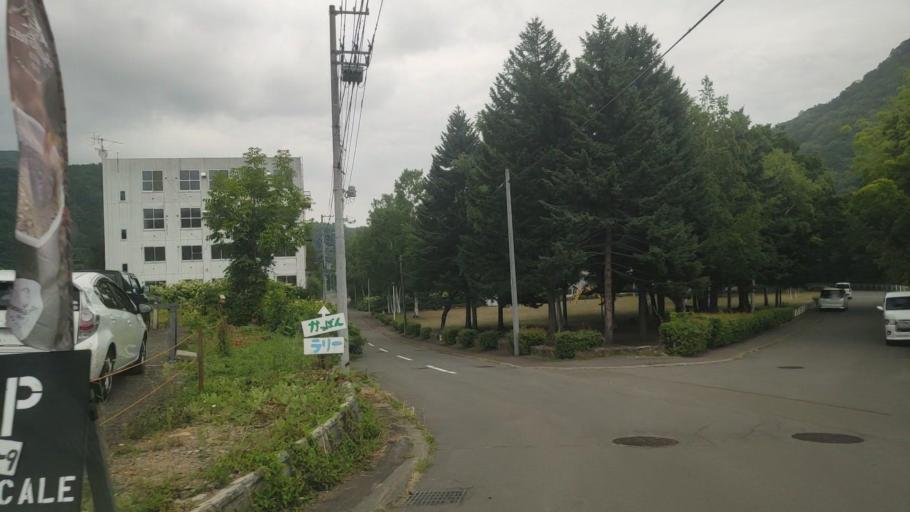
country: JP
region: Hokkaido
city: Sapporo
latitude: 42.9718
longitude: 141.1678
